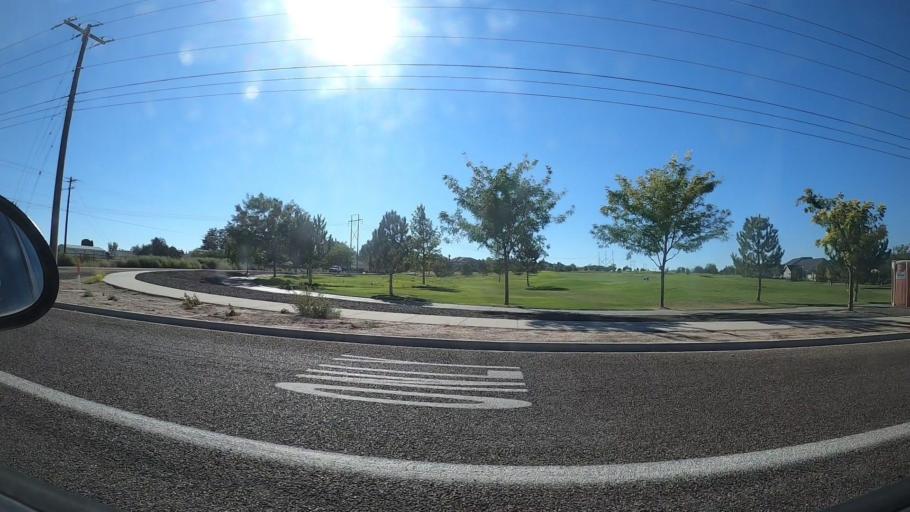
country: US
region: Idaho
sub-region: Canyon County
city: Nampa
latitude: 43.5499
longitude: -116.6127
